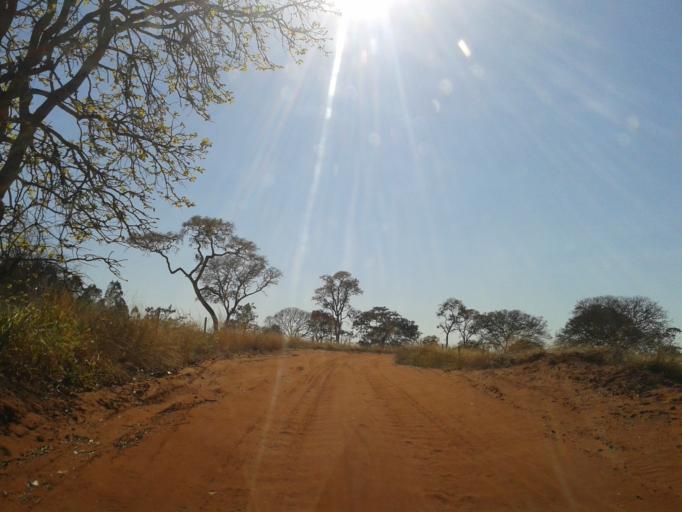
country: BR
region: Minas Gerais
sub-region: Ituiutaba
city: Ituiutaba
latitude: -19.0318
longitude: -49.3197
